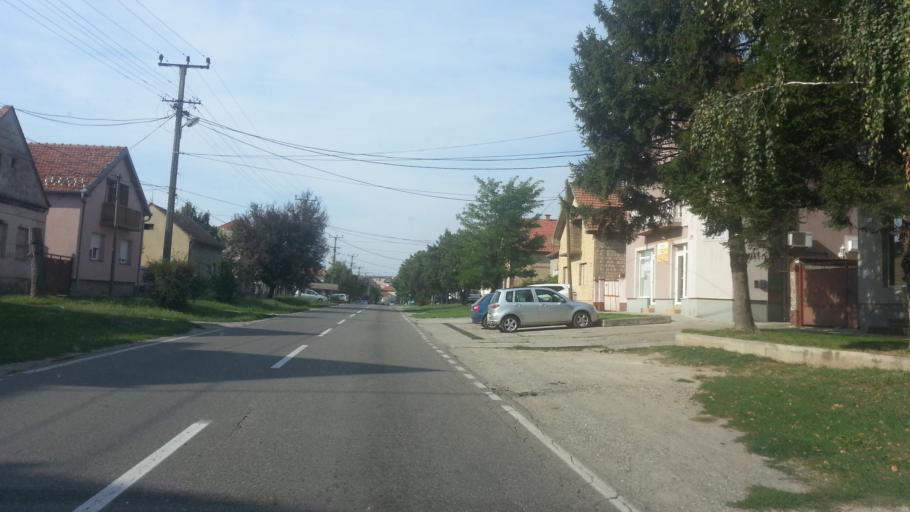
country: RS
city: Novi Banovci
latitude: 44.9526
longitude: 20.2818
